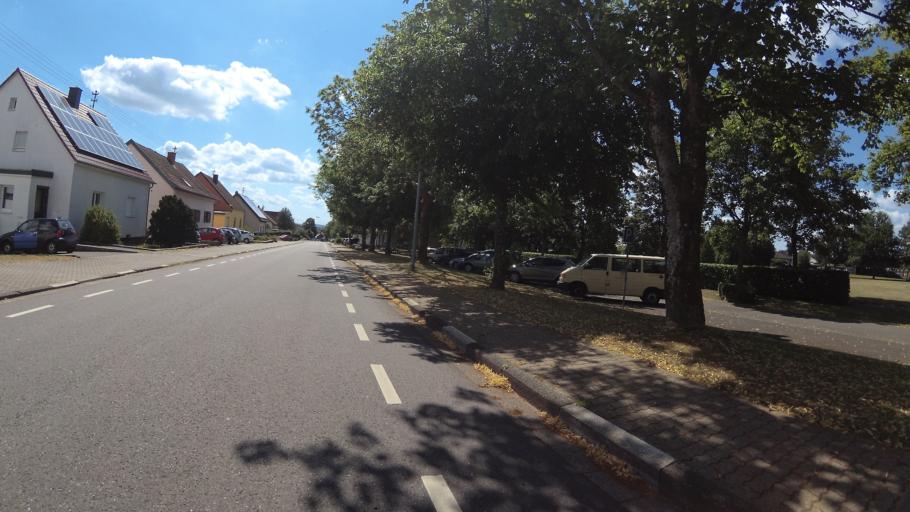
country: DE
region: Saarland
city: Weiskirchen
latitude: 49.5432
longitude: 6.7916
